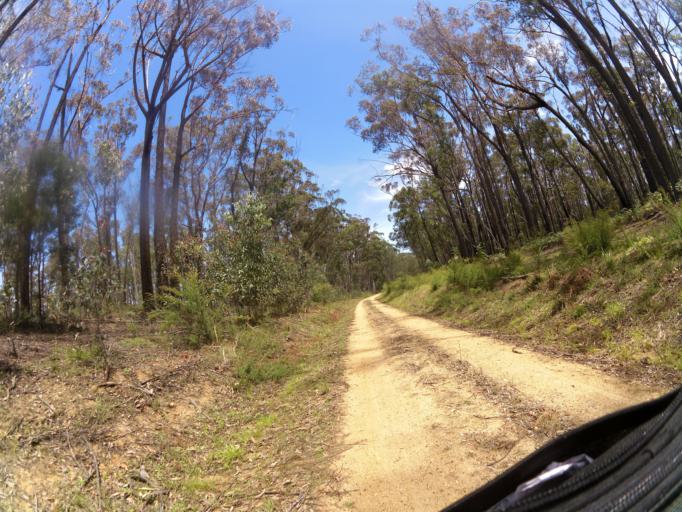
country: AU
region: Victoria
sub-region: East Gippsland
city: Lakes Entrance
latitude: -37.7553
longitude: 147.9692
